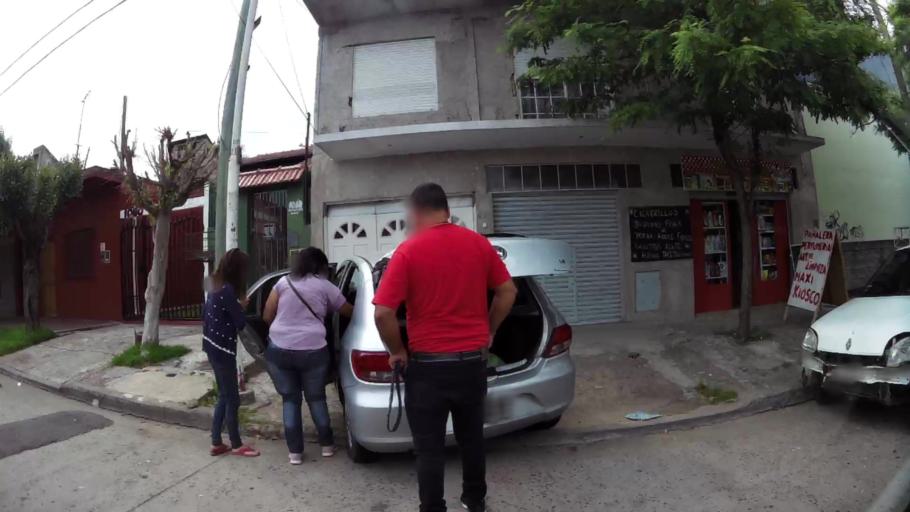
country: AR
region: Buenos Aires
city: San Justo
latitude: -34.7007
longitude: -58.5241
